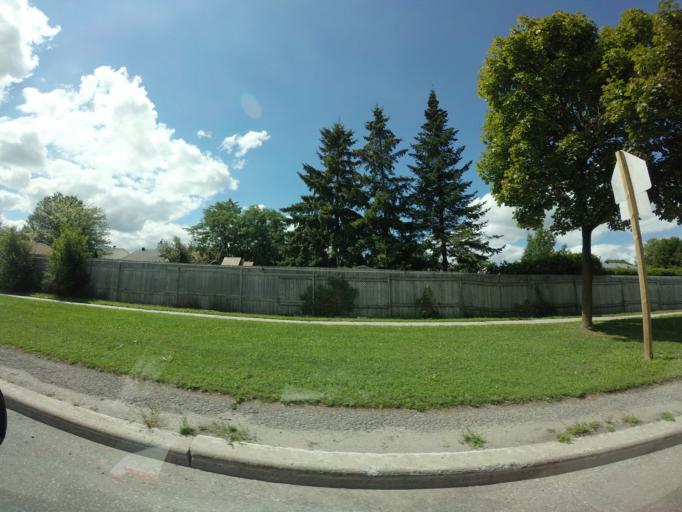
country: CA
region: Quebec
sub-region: Outaouais
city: Gatineau
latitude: 45.4716
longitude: -75.5478
